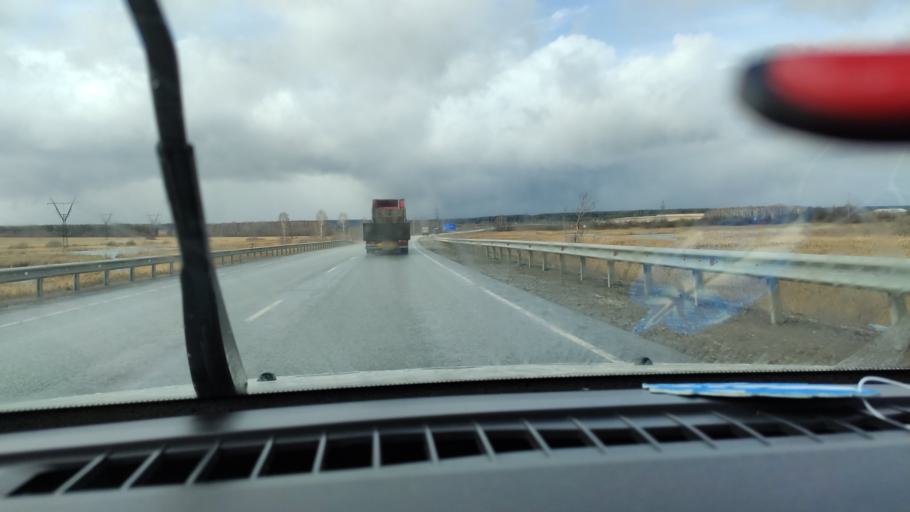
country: RU
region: Sverdlovsk
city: Achit
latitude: 56.7846
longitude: 57.8938
